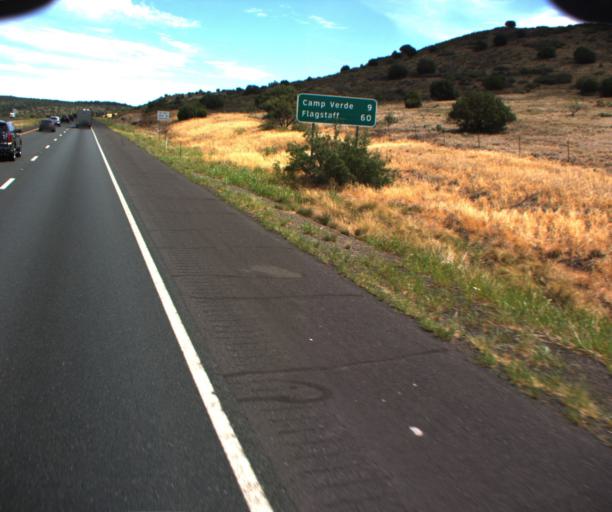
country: US
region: Arizona
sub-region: Yavapai County
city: Camp Verde
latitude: 34.5253
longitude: -111.9839
